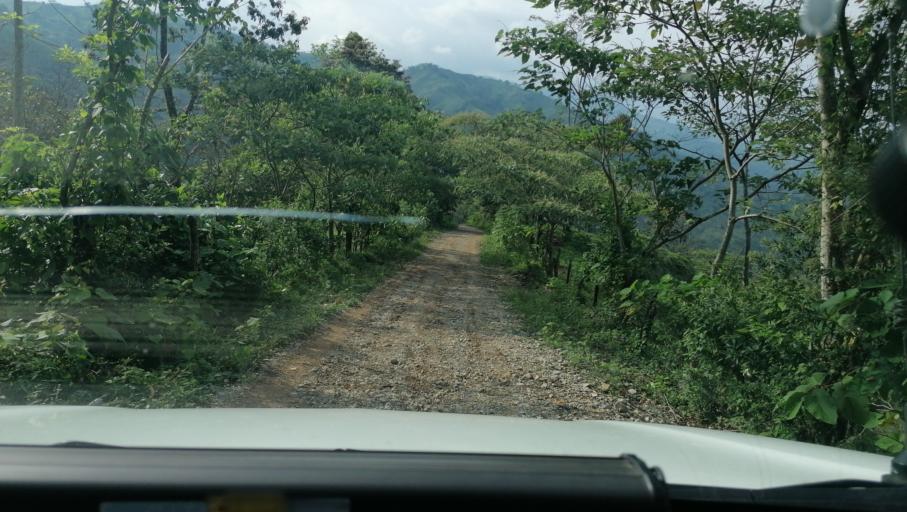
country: MX
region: Chiapas
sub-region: Tapilula
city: San Francisco Jacona
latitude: 17.3194
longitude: -93.0985
